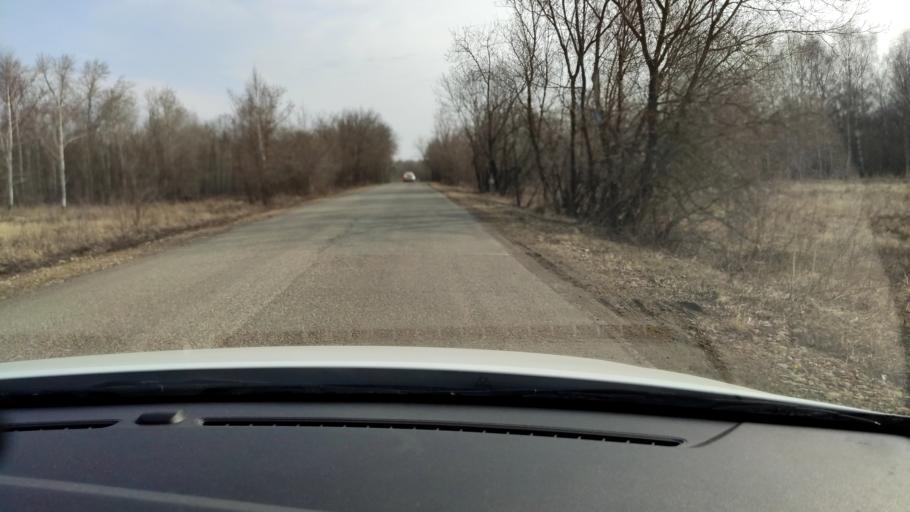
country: RU
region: Tatarstan
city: Stolbishchi
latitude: 55.7164
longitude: 49.2191
